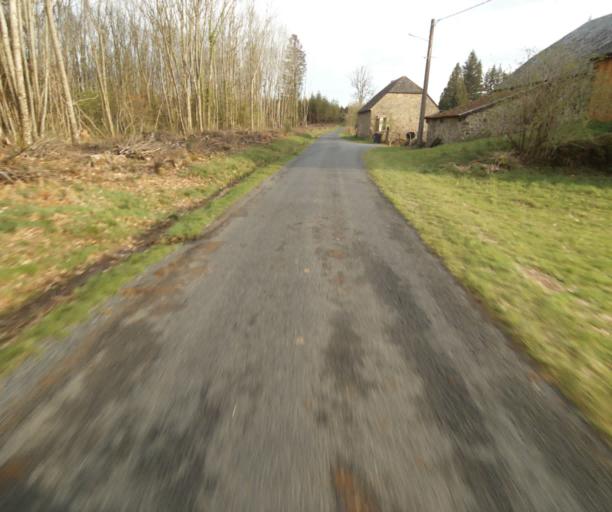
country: FR
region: Limousin
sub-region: Departement de la Correze
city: Argentat
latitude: 45.2191
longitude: 1.9395
